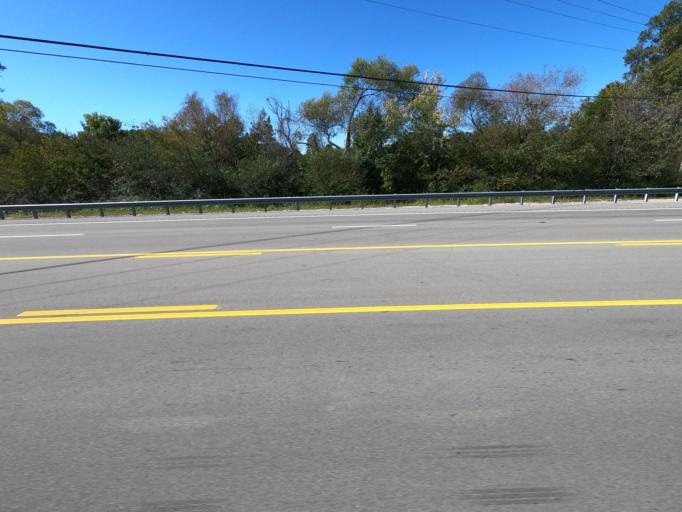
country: US
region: Tennessee
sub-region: Maury County
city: Mount Pleasant
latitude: 35.4404
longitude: -87.2794
